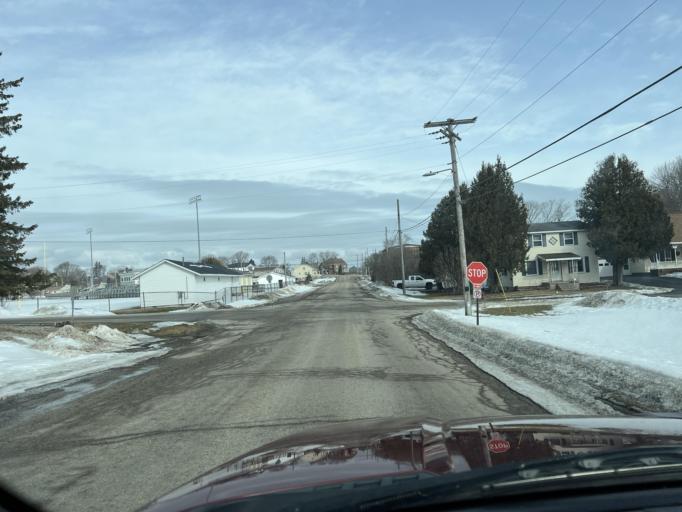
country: US
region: Michigan
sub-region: Mackinac County
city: Saint Ignace
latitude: 45.8640
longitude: -84.7243
